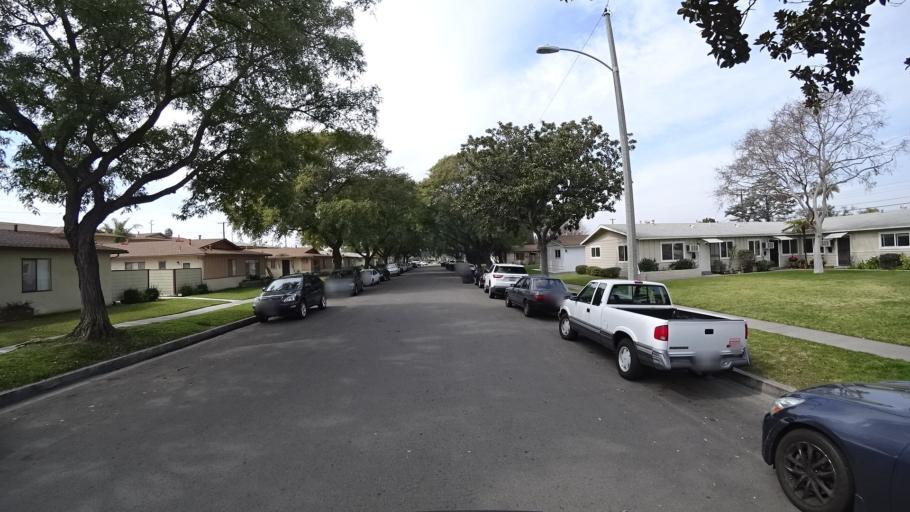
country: US
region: California
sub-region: Orange County
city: Stanton
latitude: 33.8187
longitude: -117.9553
